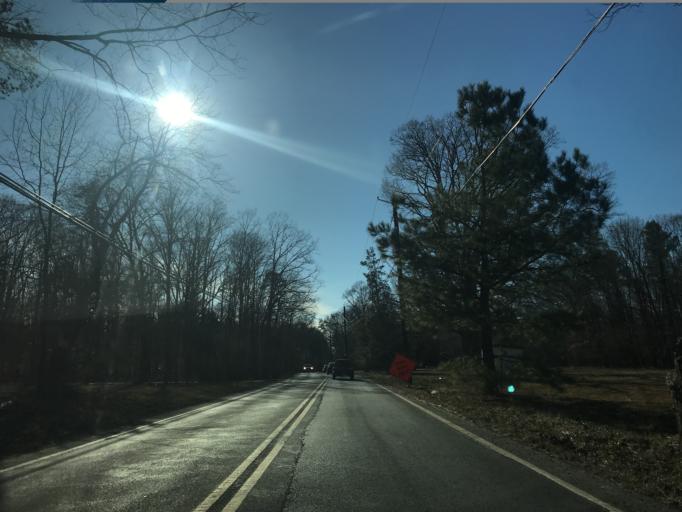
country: US
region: Maryland
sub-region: Charles County
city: Waldorf
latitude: 38.6846
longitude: -76.9248
